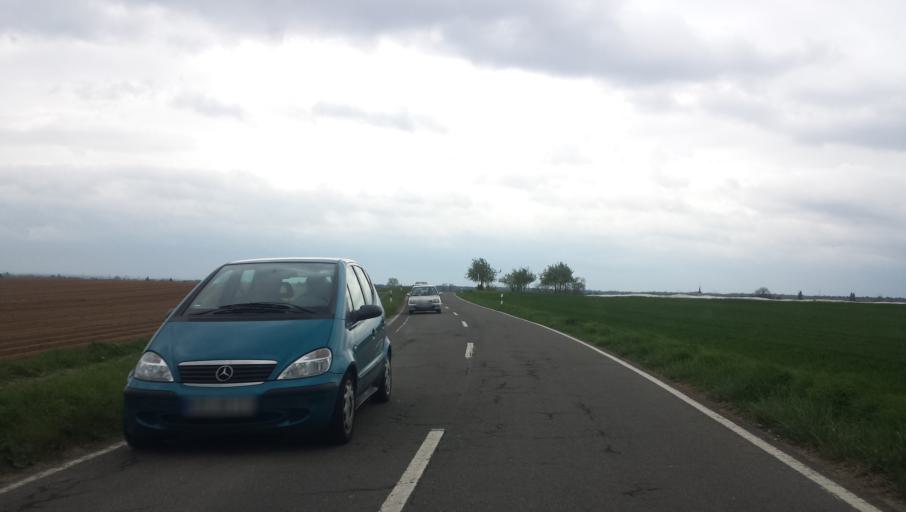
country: DE
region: Rheinland-Pfalz
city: Schwegenheim
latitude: 49.2603
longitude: 8.3237
